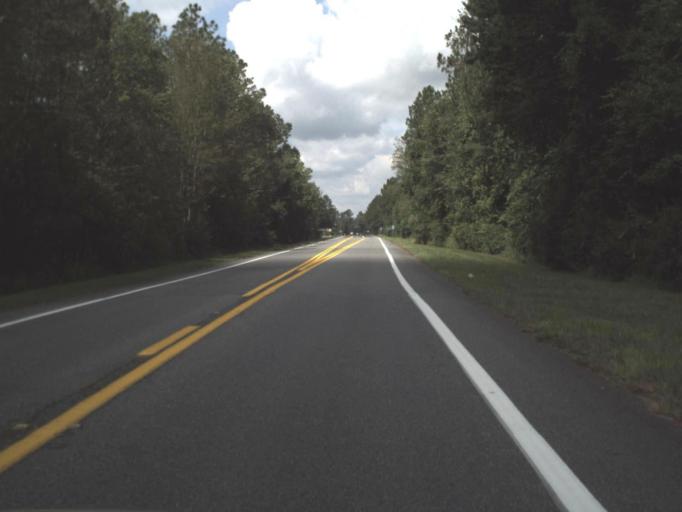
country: US
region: Florida
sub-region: Union County
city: Lake Butler
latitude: 30.0726
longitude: -82.2211
